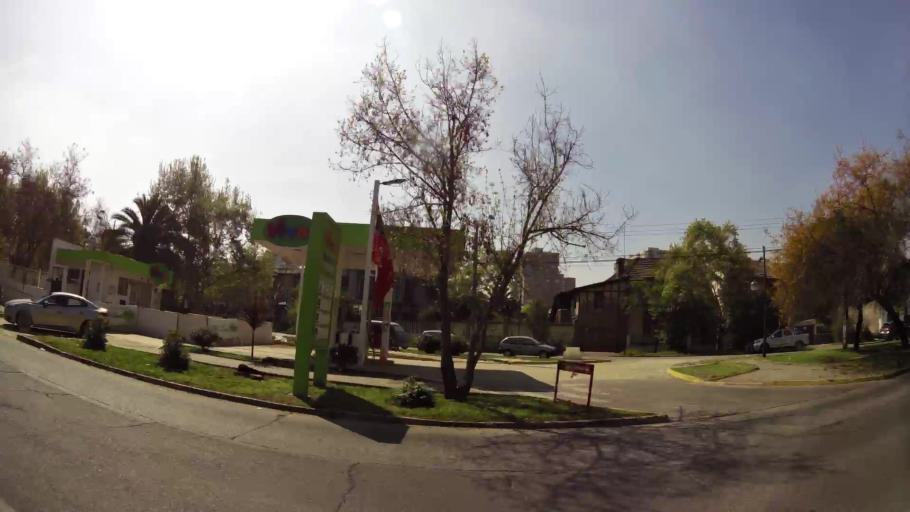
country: CL
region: Santiago Metropolitan
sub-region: Provincia de Santiago
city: Santiago
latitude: -33.4558
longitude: -70.6188
